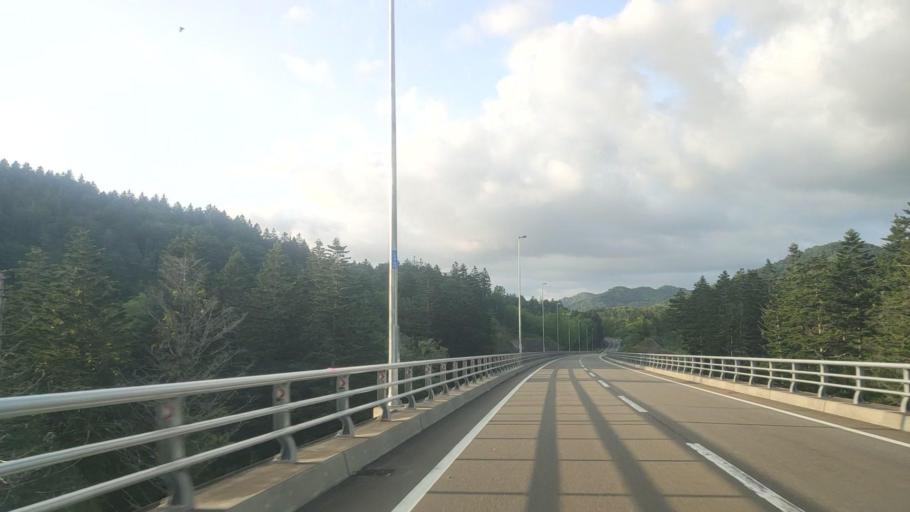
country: JP
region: Hokkaido
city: Bibai
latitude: 43.1077
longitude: 142.0982
